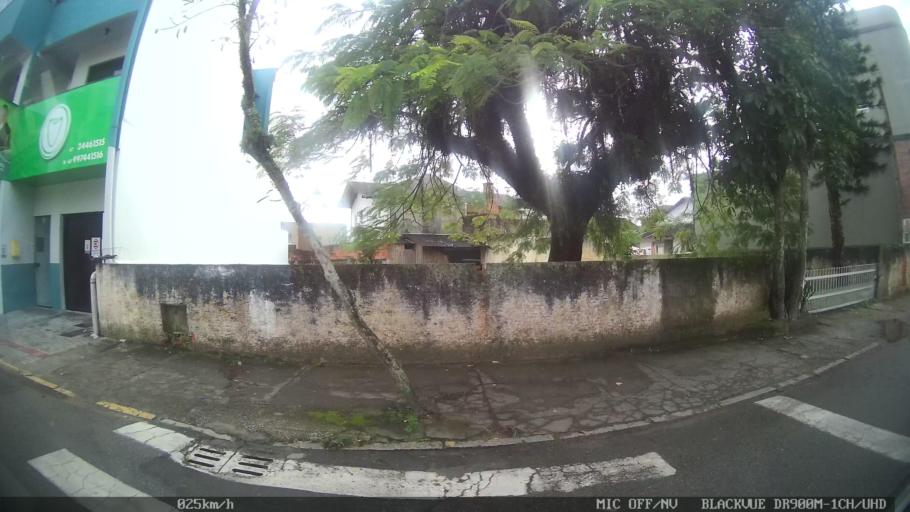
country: BR
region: Santa Catarina
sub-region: Barra Velha
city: Barra Velha
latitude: -26.6323
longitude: -48.6856
